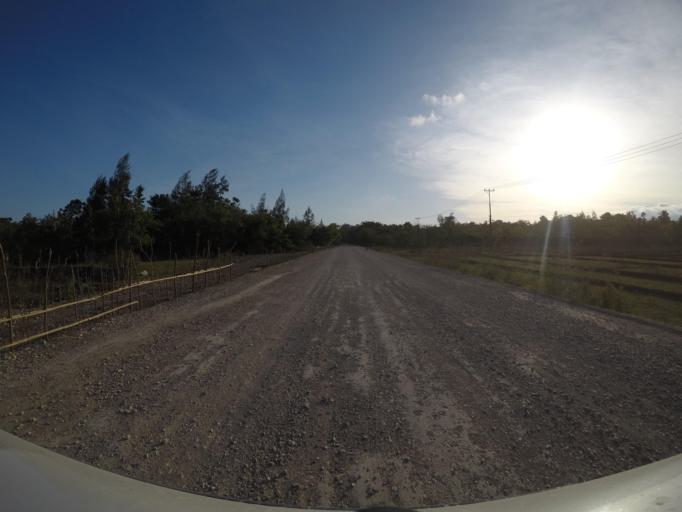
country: TL
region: Viqueque
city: Viqueque
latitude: -8.8303
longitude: 126.5234
